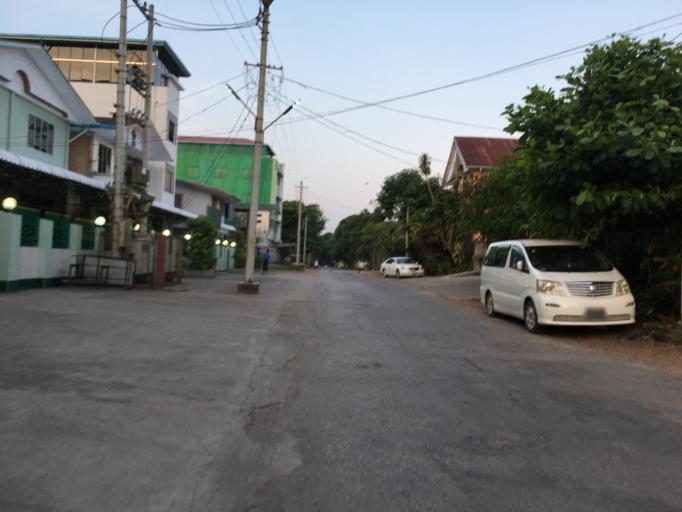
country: MM
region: Mon
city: Mawlamyine
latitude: 16.4781
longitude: 97.6235
